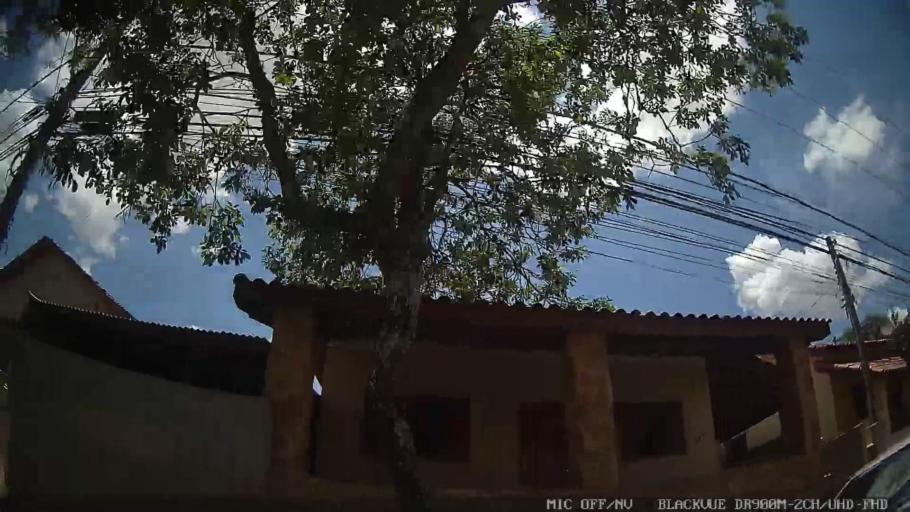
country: BR
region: Sao Paulo
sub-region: Itatiba
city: Itatiba
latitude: -22.8743
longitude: -46.7905
